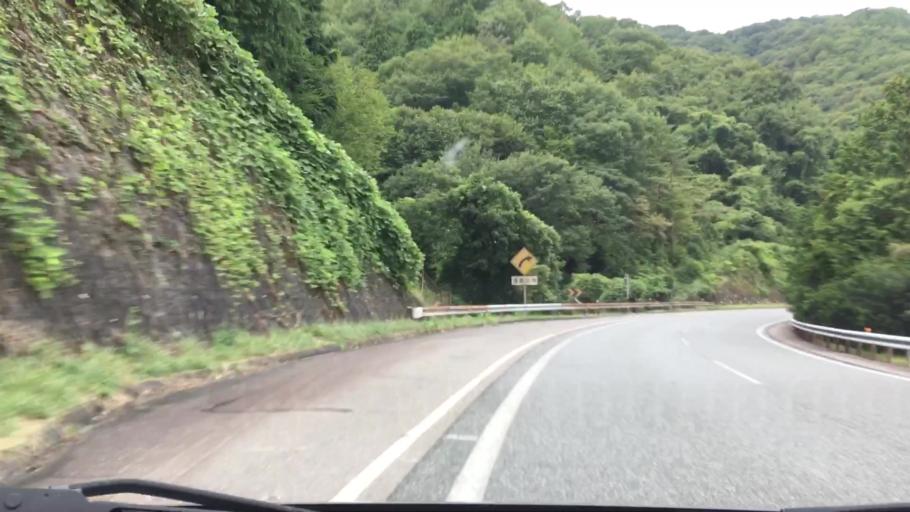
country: JP
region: Okayama
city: Niimi
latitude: 34.9864
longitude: 133.6083
